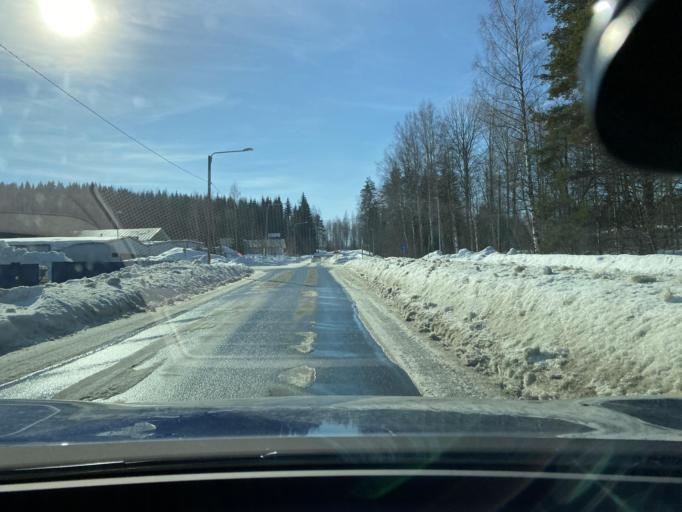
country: FI
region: Central Finland
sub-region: Jyvaeskylae
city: Muurame
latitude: 62.0998
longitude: 25.6463
